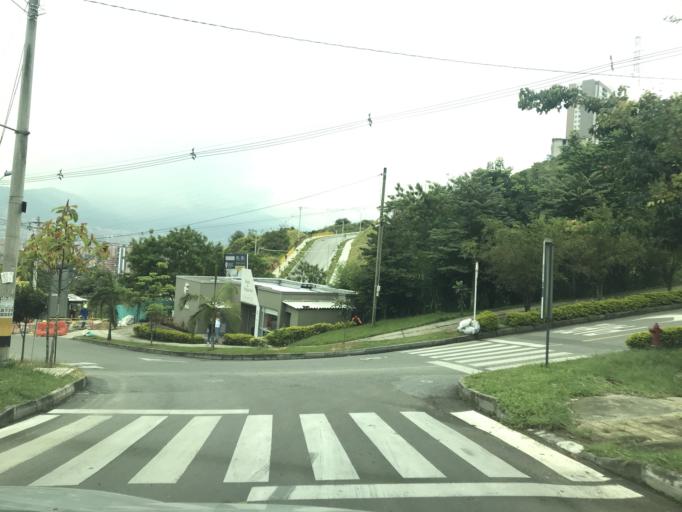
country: CO
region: Antioquia
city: Medellin
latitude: 6.2695
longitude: -75.6069
